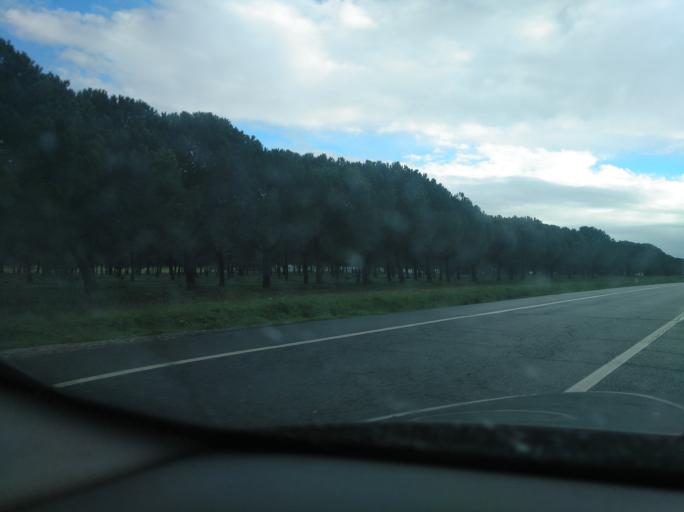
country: PT
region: Beja
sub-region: Aljustrel
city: Aljustrel
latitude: 37.9555
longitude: -8.3812
